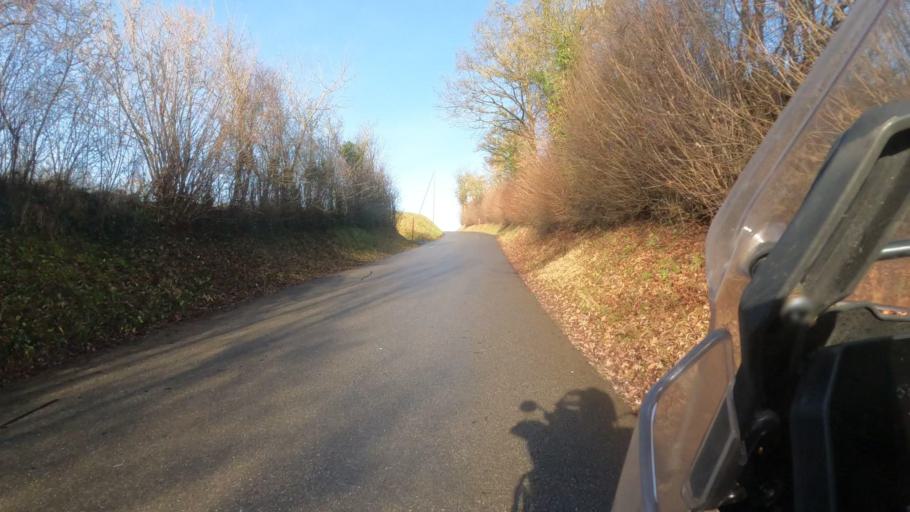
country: CH
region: Schaffhausen
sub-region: Bezirk Reiat
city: Thayngen
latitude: 47.7561
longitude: 8.7039
